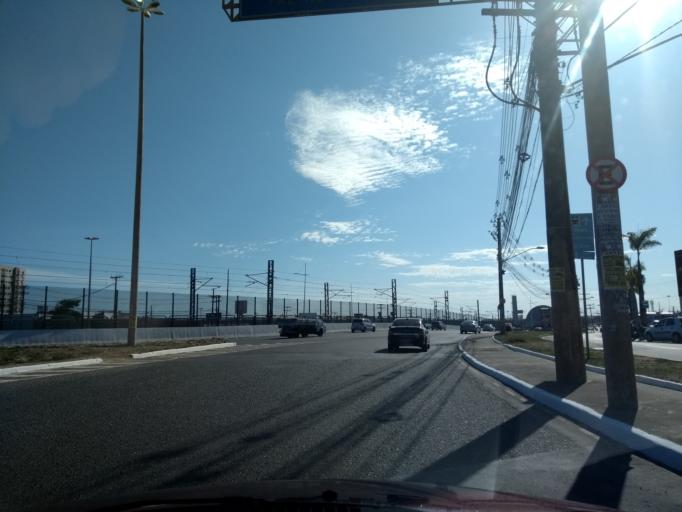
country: BR
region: Bahia
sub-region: Lauro De Freitas
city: Lauro de Freitas
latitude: -12.9203
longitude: -38.3549
